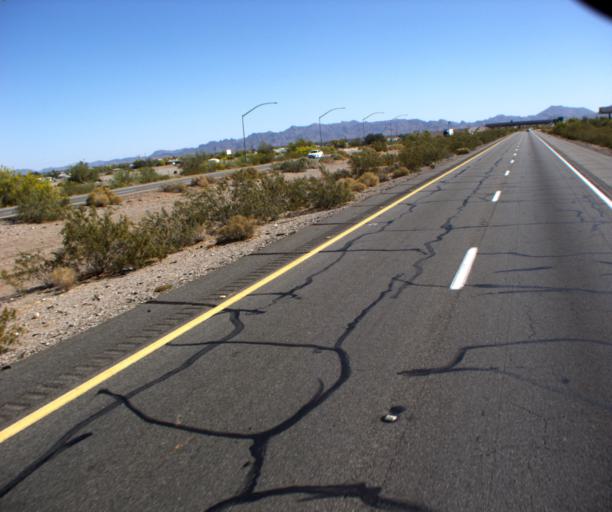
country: US
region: Arizona
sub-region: La Paz County
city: Quartzsite
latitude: 33.6640
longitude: -114.2097
